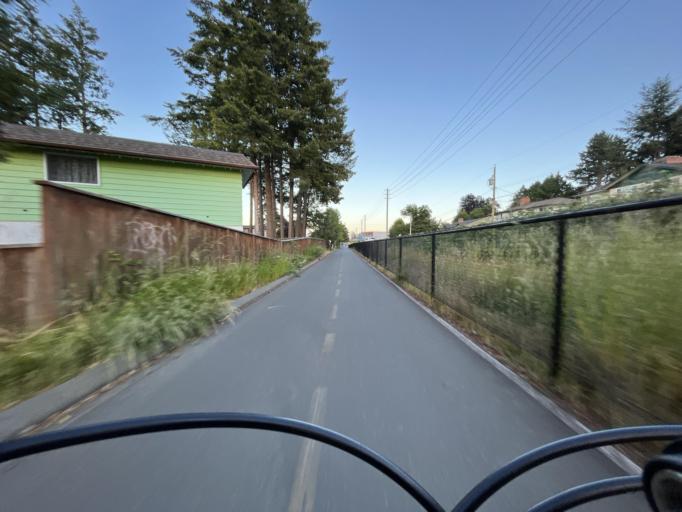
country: CA
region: British Columbia
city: Victoria
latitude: 48.4376
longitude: -123.4044
